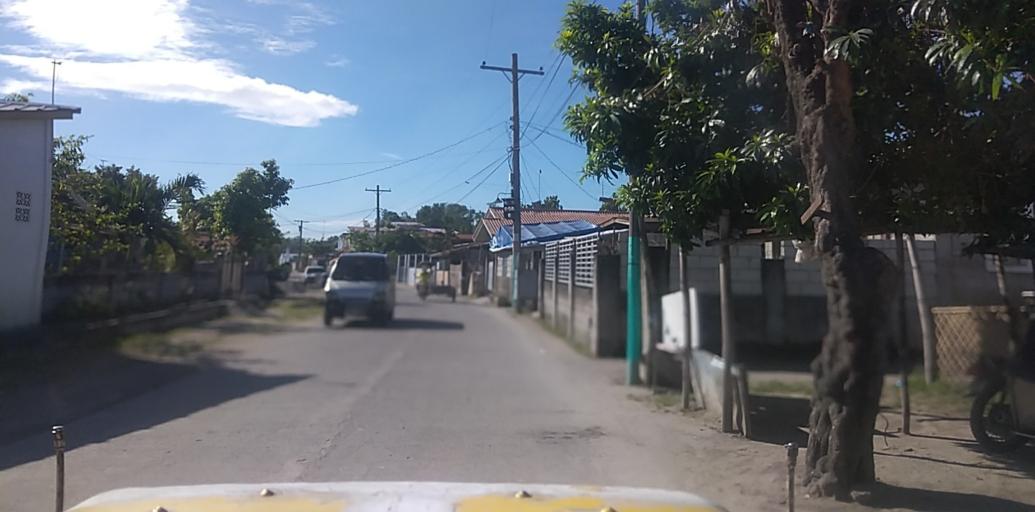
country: PH
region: Central Luzon
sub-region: Province of Pampanga
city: San Patricio
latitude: 15.1111
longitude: 120.7118
